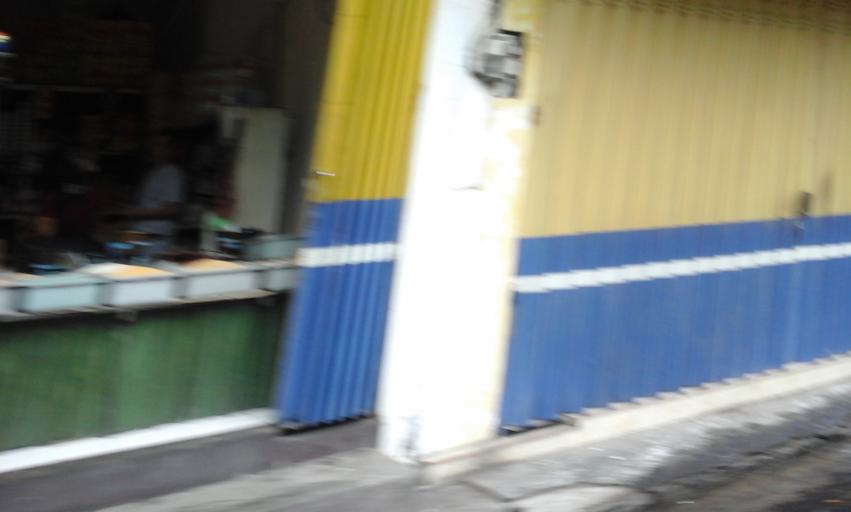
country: ID
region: East Java
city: Lumajang
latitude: -8.1301
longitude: 113.2251
